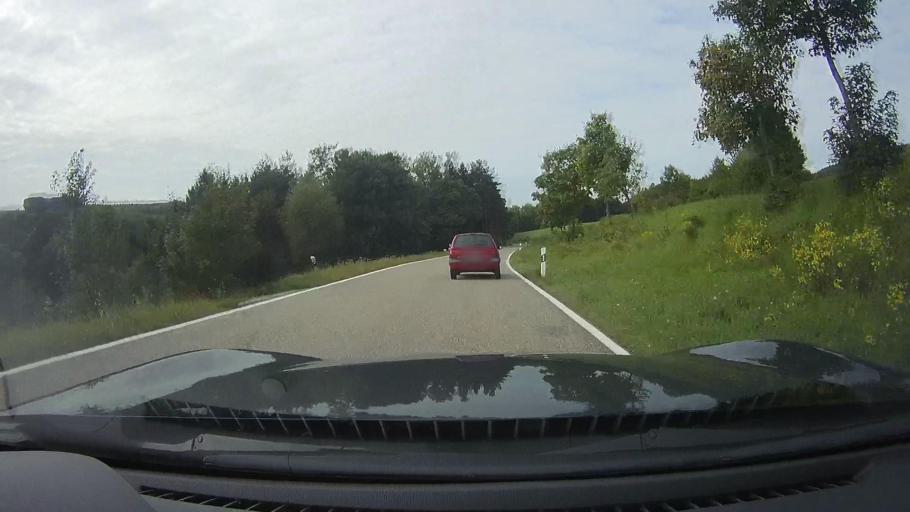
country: DE
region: Baden-Wuerttemberg
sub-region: Regierungsbezirk Stuttgart
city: Lowenstein
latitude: 49.0707
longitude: 9.3689
